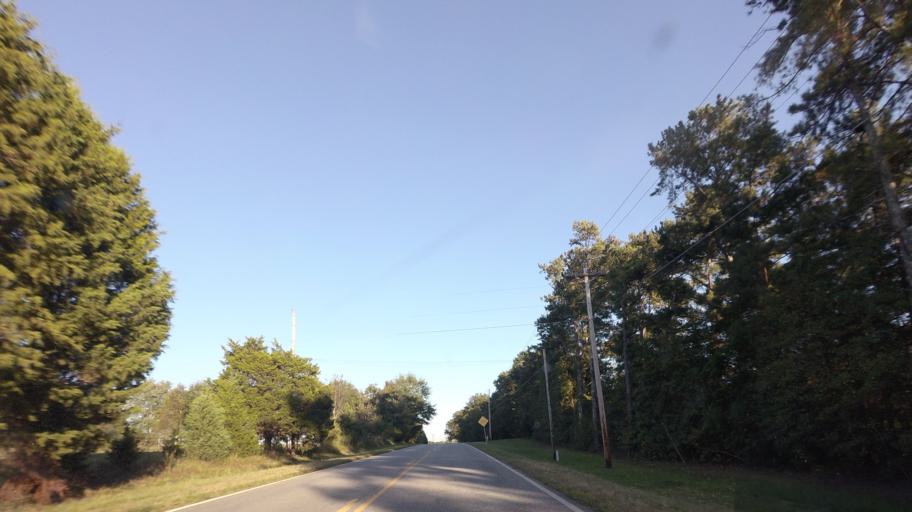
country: US
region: Georgia
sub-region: Henry County
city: Locust Grove
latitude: 33.2833
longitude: -84.1560
